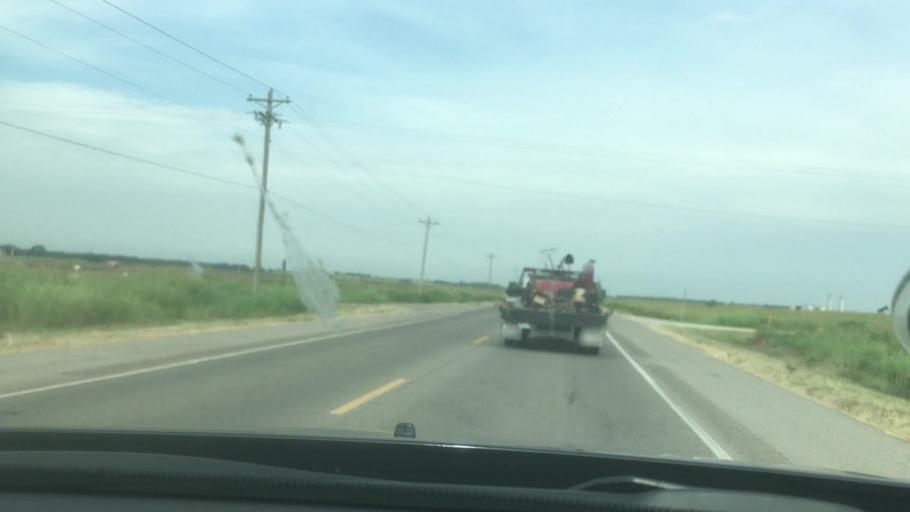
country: US
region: Oklahoma
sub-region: Garvin County
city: Lindsay
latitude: 34.8231
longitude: -97.5272
